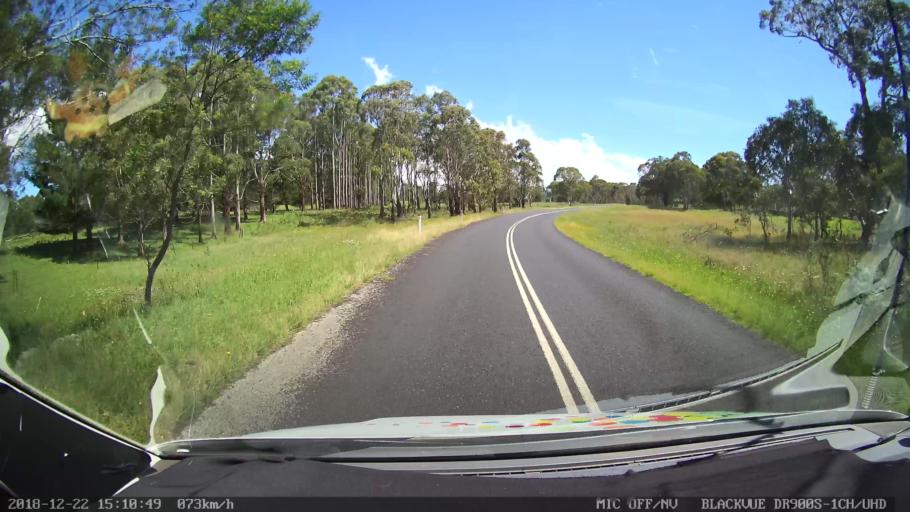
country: AU
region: New South Wales
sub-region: Bellingen
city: Dorrigo
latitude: -30.3390
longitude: 152.4065
